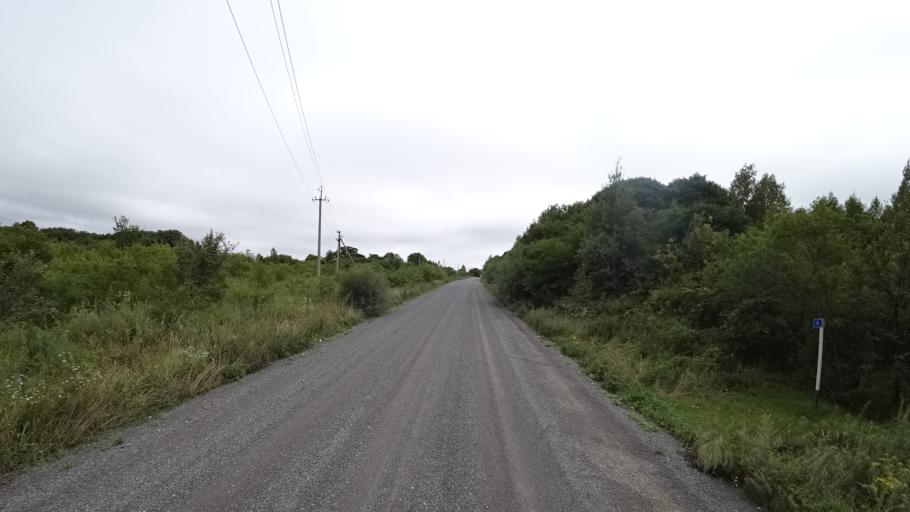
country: RU
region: Primorskiy
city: Lyalichi
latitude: 44.0727
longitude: 132.4762
